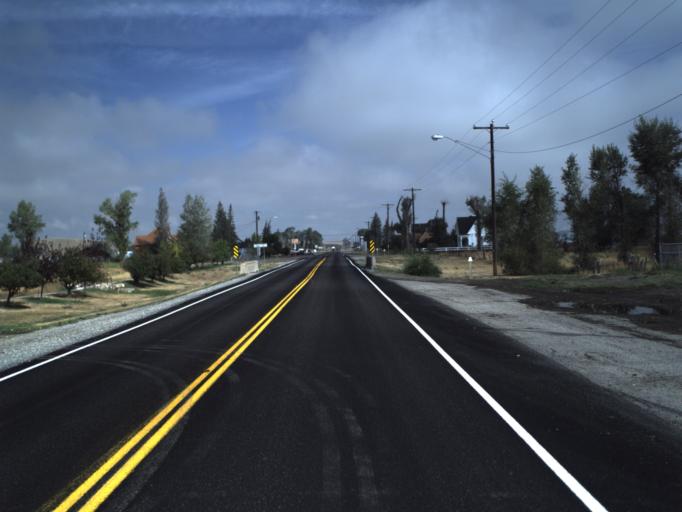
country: US
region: Utah
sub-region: Rich County
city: Randolph
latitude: 41.5203
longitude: -111.1629
